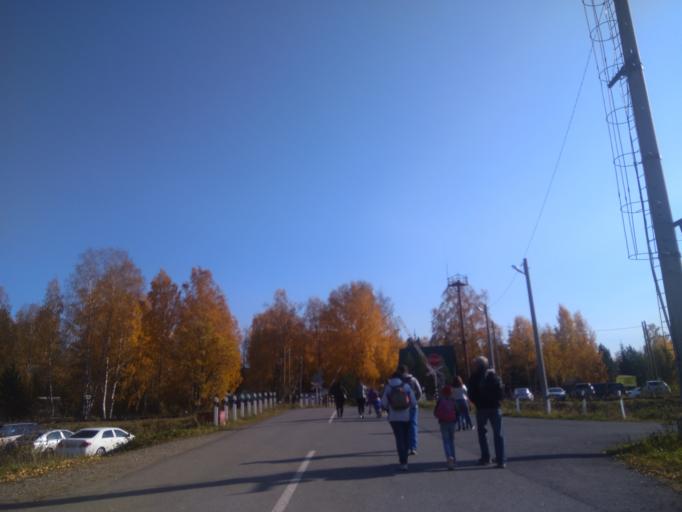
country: RU
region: Sverdlovsk
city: Mikhaylovsk
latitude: 56.5250
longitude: 59.2285
